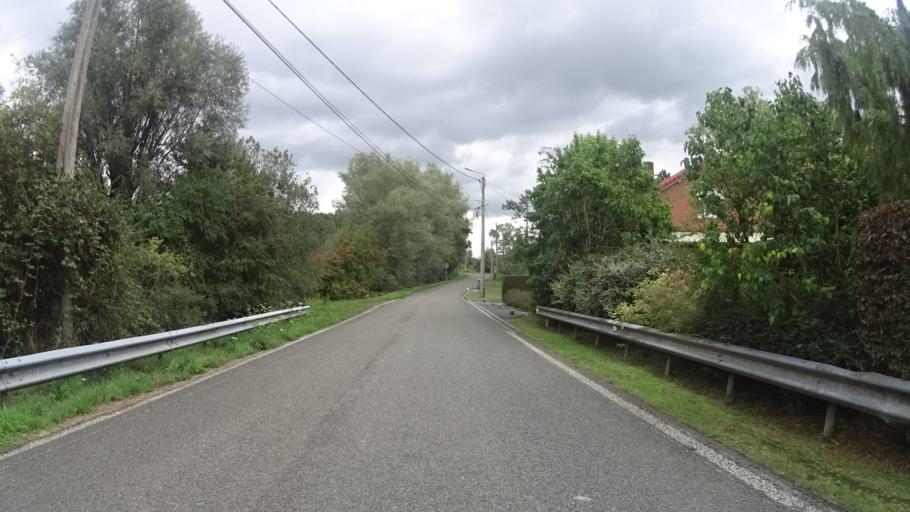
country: FR
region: Nord-Pas-de-Calais
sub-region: Departement du Nord
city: Maroilles
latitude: 50.1568
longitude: 3.7440
